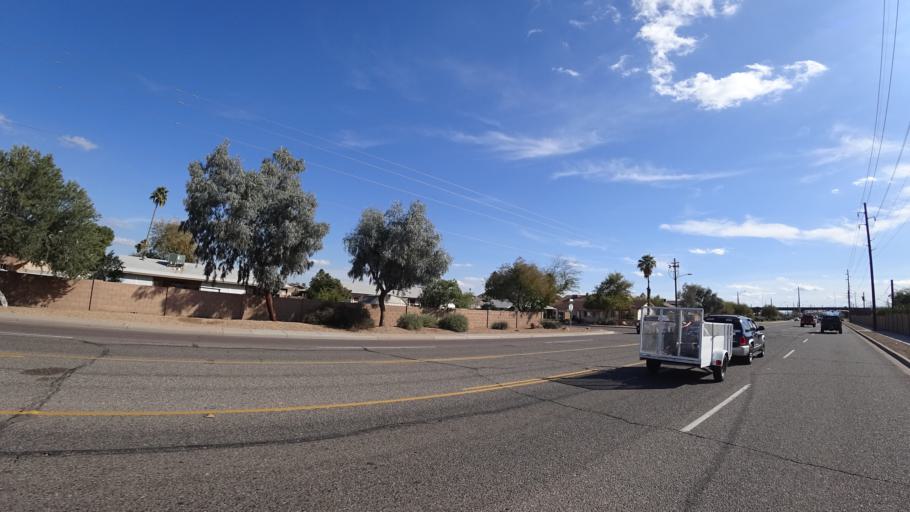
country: US
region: Arizona
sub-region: Maricopa County
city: Peoria
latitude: 33.5705
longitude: -112.2204
